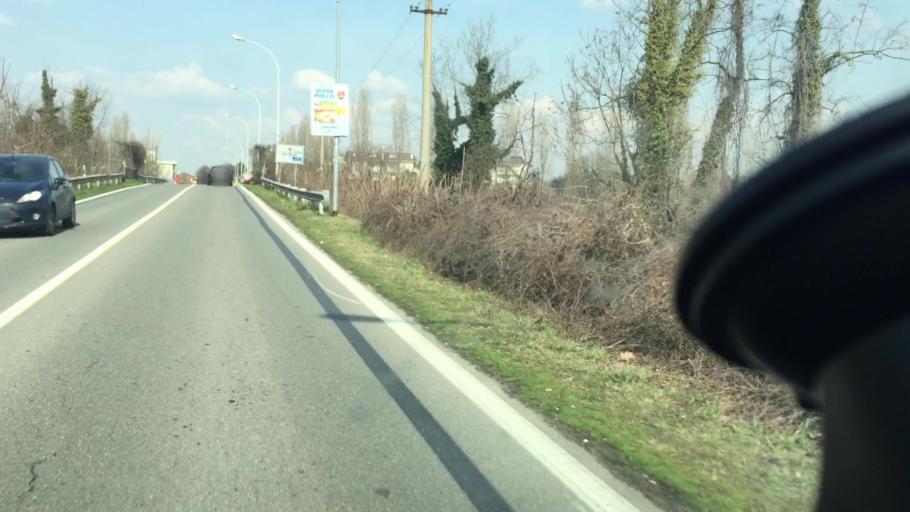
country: IT
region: Lombardy
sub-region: Citta metropolitana di Milano
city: Cernusco sul Naviglio
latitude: 45.5205
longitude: 9.3377
